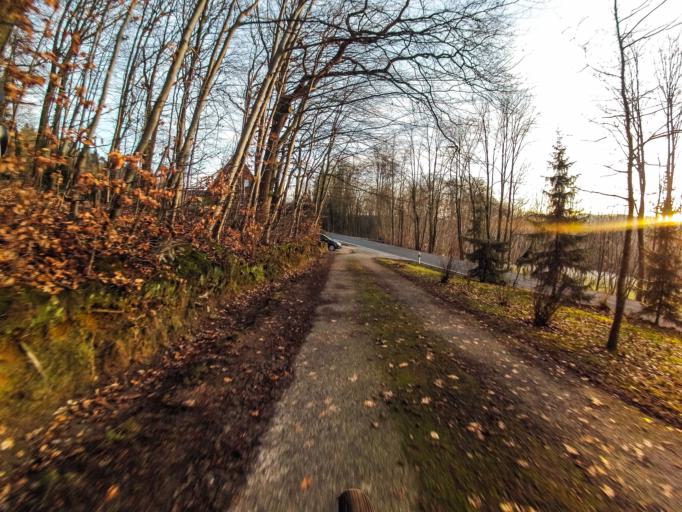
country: DE
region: North Rhine-Westphalia
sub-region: Regierungsbezirk Munster
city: Westerkappeln
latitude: 52.2894
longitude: 7.8364
